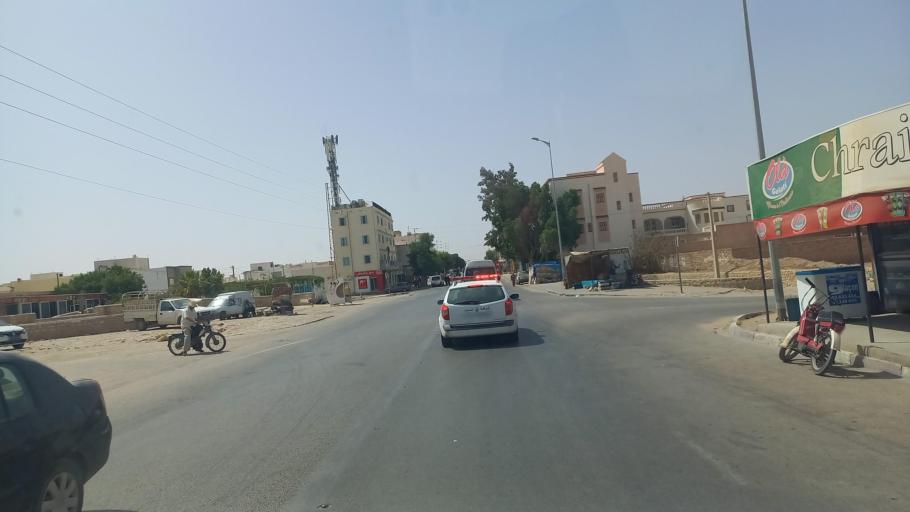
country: TN
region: Madanin
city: Medenine
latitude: 33.3296
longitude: 10.4851
